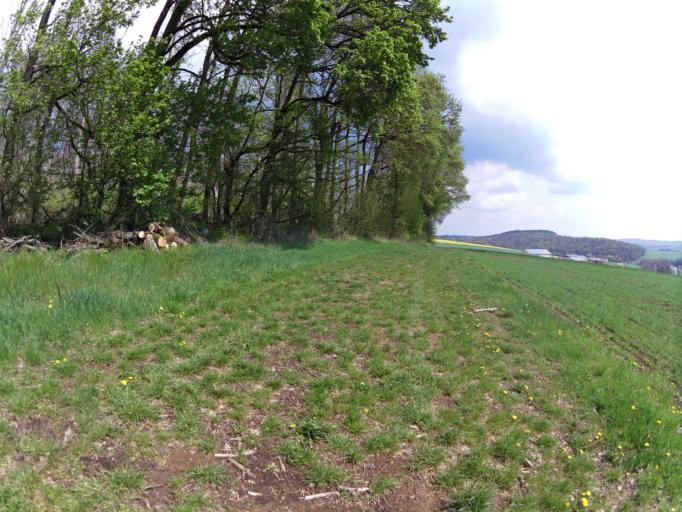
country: DE
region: Bavaria
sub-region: Regierungsbezirk Unterfranken
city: Waldbrunn
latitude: 49.7835
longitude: 9.7921
